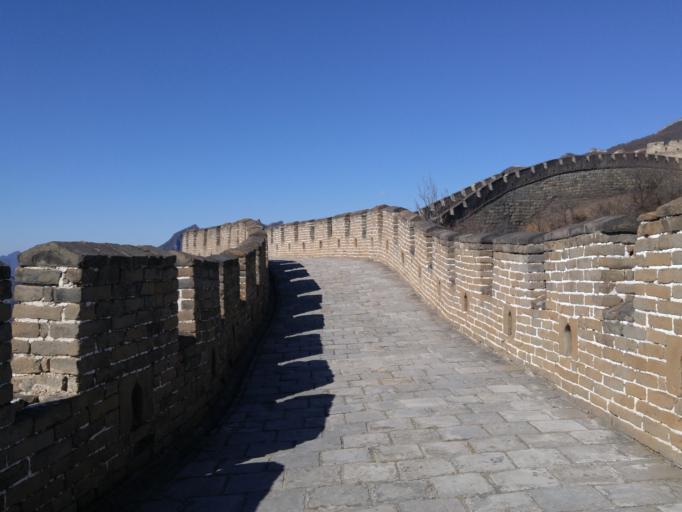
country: CN
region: Beijing
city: Bohai
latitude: 40.4411
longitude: 116.5587
